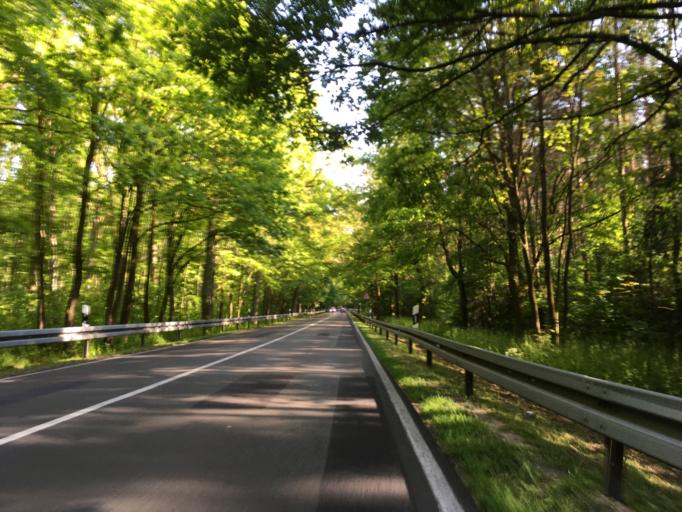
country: DE
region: Brandenburg
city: Protzel
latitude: 52.6133
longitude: 13.9553
